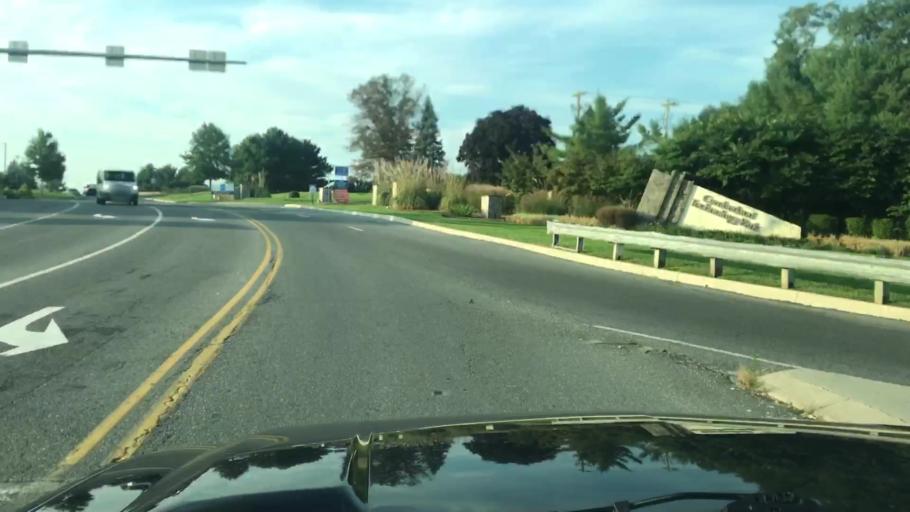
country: US
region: Pennsylvania
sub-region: Cumberland County
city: Enola
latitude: 40.2883
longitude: -76.9770
